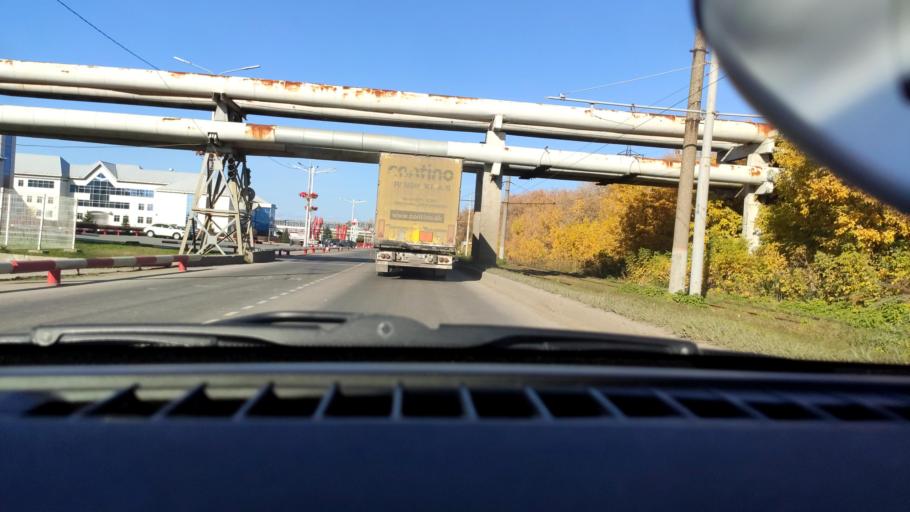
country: RU
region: Perm
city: Gamovo
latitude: 57.9222
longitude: 56.1422
